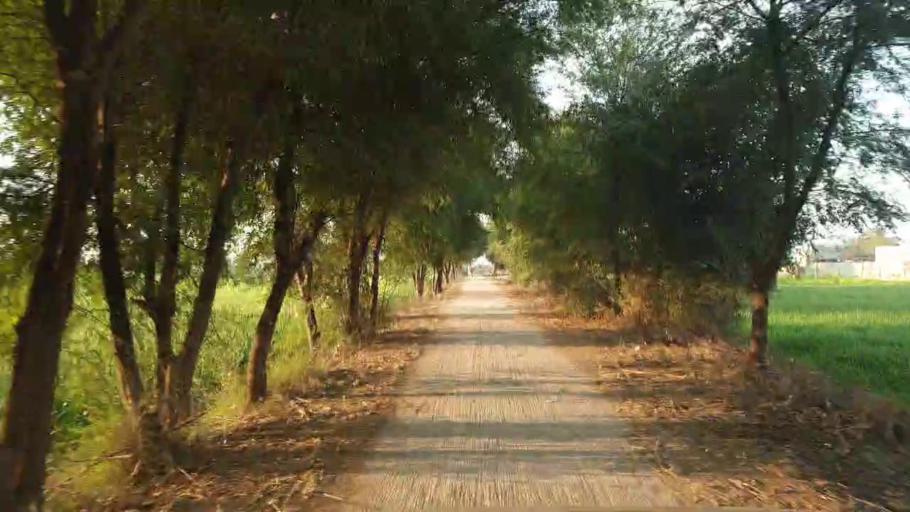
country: PK
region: Sindh
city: Shahpur Chakar
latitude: 26.1713
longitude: 68.6241
